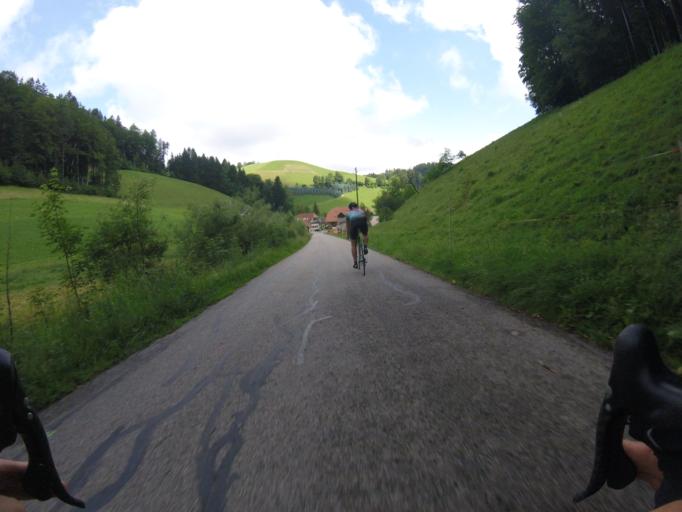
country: CH
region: Bern
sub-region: Emmental District
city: Krauchthal
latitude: 46.9882
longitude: 7.5819
